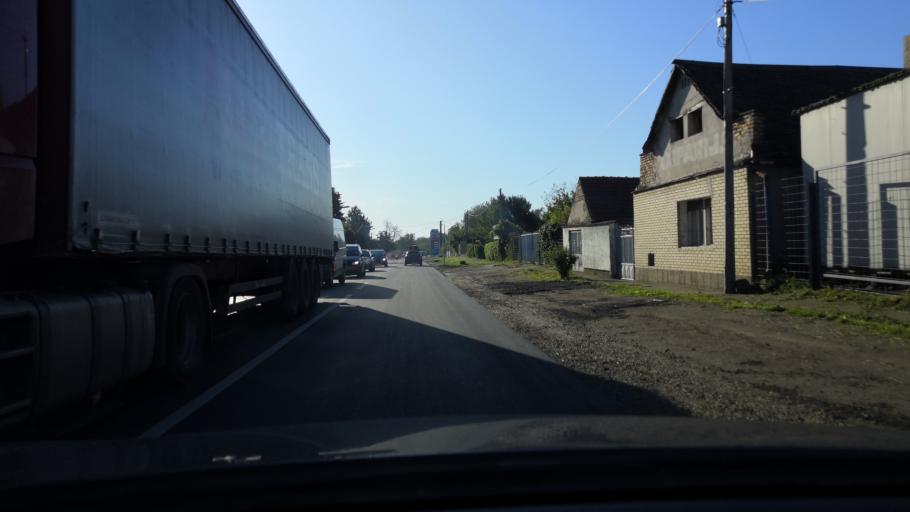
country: RS
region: Autonomna Pokrajina Vojvodina
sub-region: Juznobacki Okrug
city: Petrovaradin
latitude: 45.2330
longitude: 19.8916
